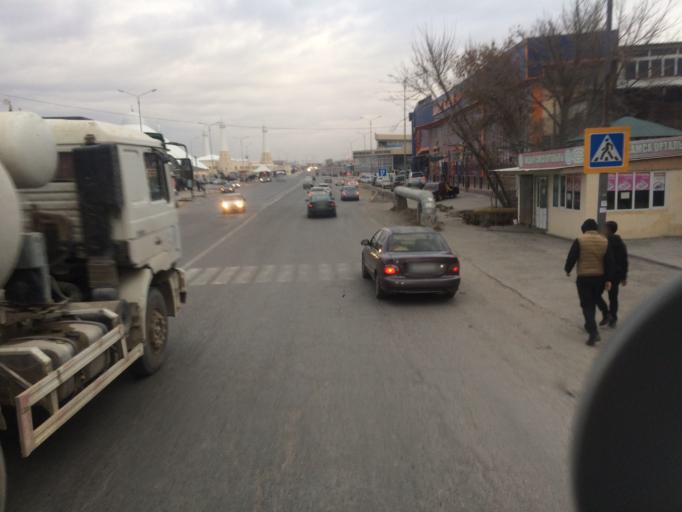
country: KZ
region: Ongtustik Qazaqstan
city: Shymkent
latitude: 42.3486
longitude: 69.5282
